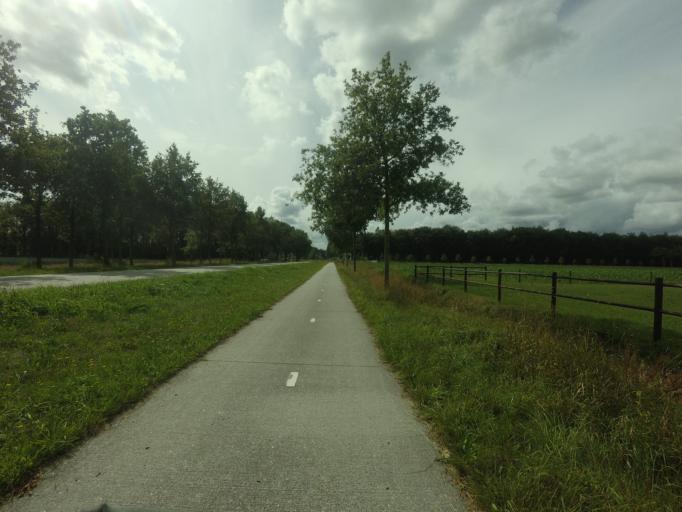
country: NL
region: Groningen
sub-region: Gemeente Leek
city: Leek
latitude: 53.0252
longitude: 6.4137
